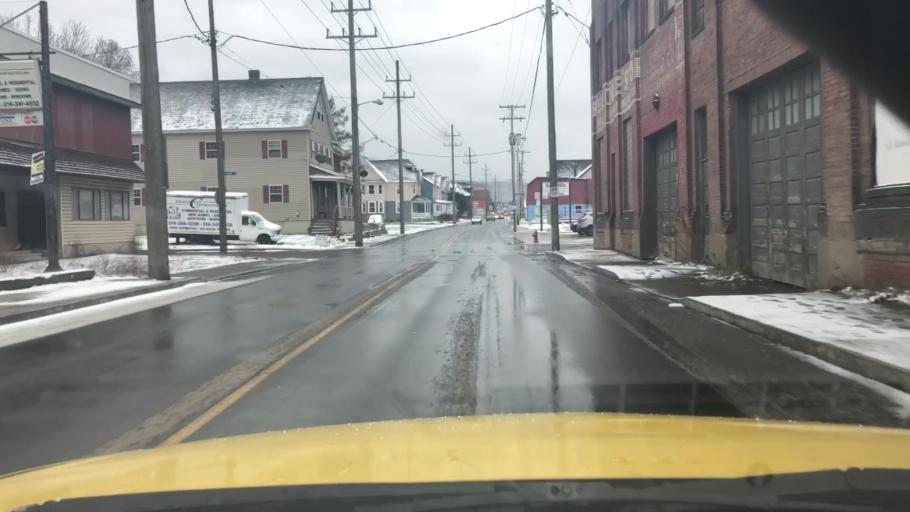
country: US
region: Pennsylvania
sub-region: Cambria County
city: Dale
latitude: 40.3130
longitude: -78.9123
